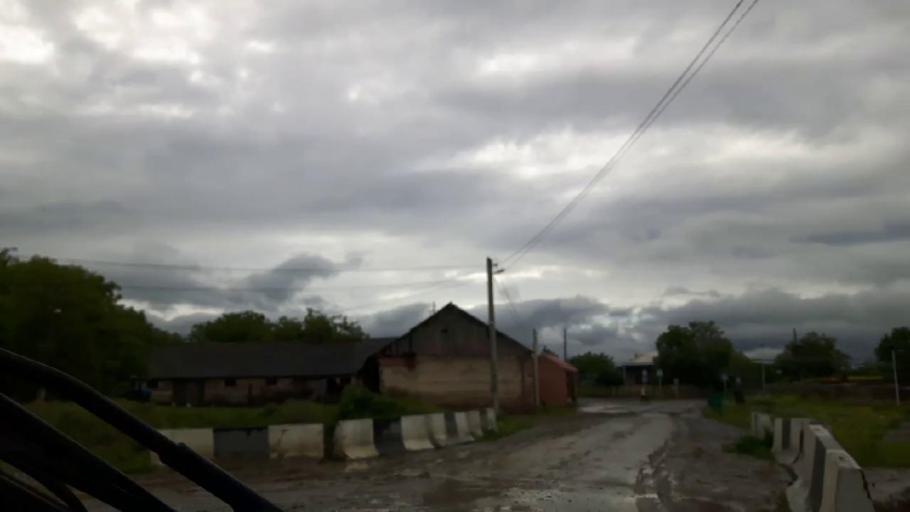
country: GE
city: Agara
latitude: 41.9943
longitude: 43.7341
